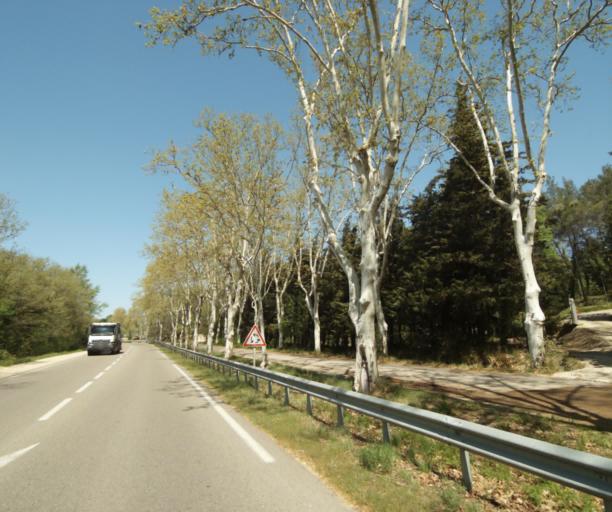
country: FR
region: Languedoc-Roussillon
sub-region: Departement de l'Herault
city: Prades-le-Lez
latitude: 43.6823
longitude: 3.8649
